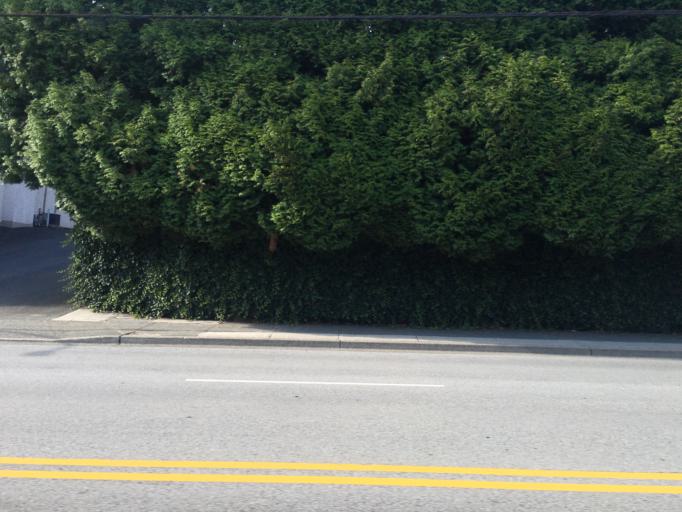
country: CA
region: British Columbia
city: Port Moody
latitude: 49.2490
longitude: -122.8396
